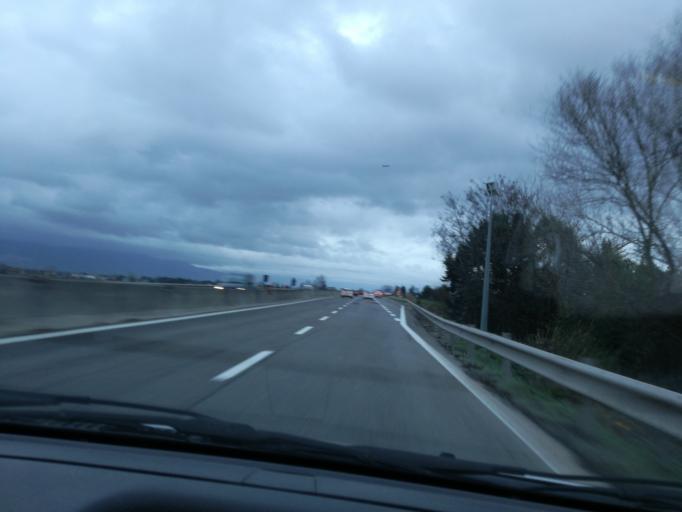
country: IT
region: Umbria
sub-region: Provincia di Perugia
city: Via Lippia
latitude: 43.0859
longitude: 12.4839
